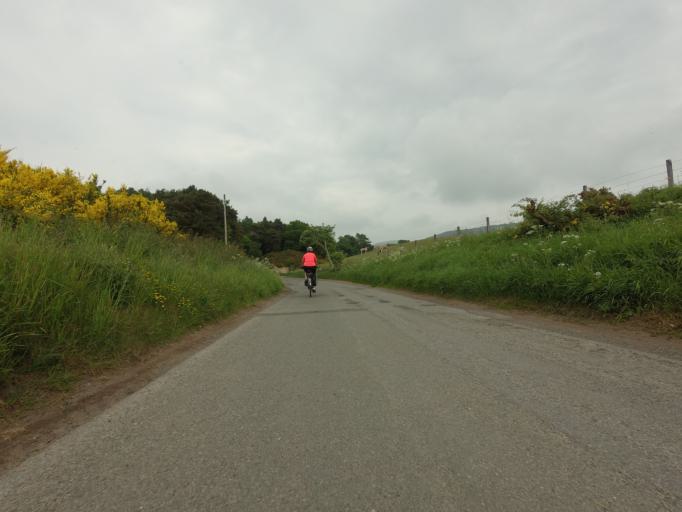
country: GB
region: Scotland
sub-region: Fife
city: Ballingry
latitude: 56.2277
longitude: -3.3408
